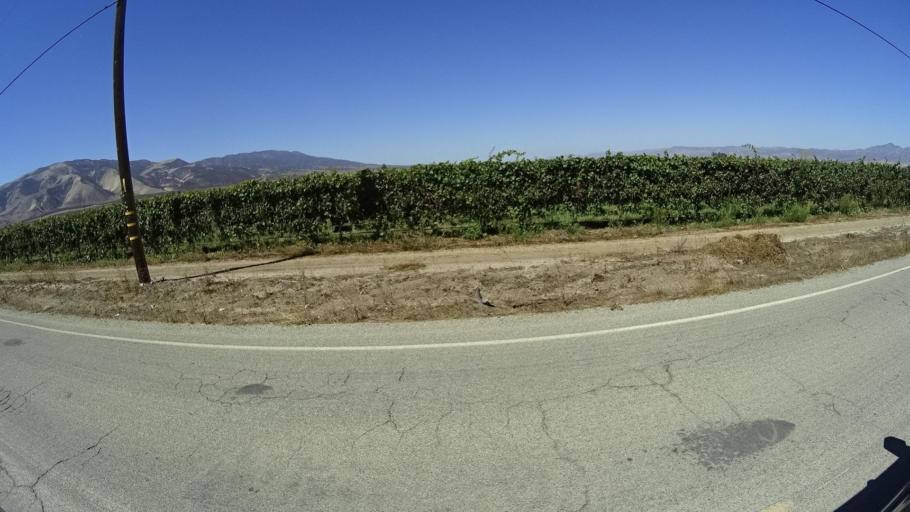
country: US
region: California
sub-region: Monterey County
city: Greenfield
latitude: 36.2938
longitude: -121.2824
